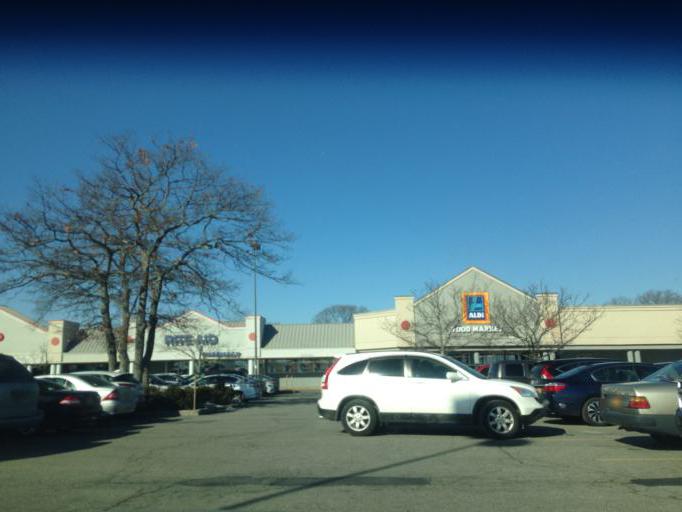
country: US
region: New York
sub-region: Suffolk County
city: Patchogue
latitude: 40.7780
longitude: -73.0332
